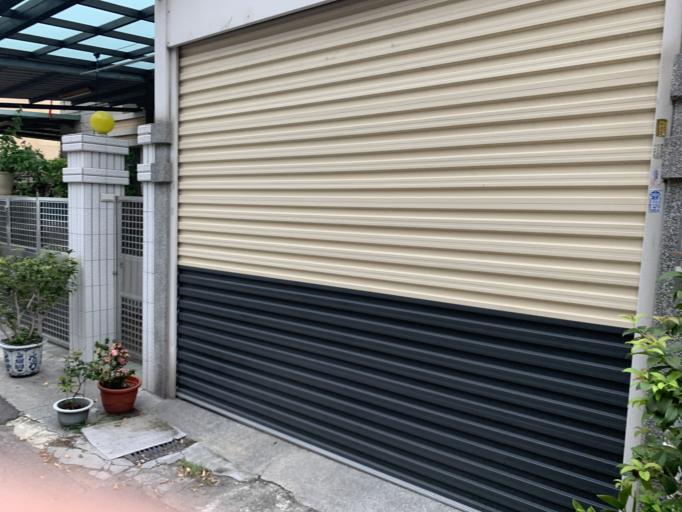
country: TW
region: Taiwan
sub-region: Taichung City
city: Taichung
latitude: 24.1551
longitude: 120.6508
